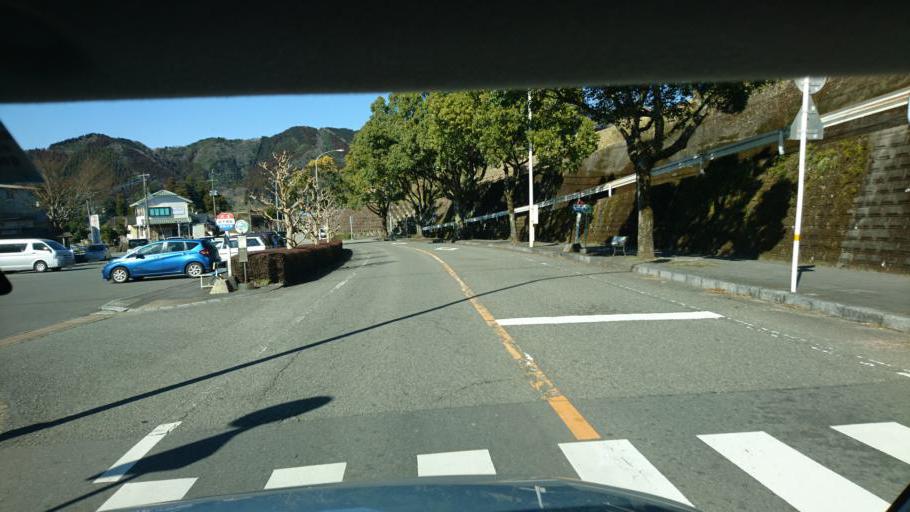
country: JP
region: Oita
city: Takedamachi
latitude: 32.7146
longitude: 131.3075
